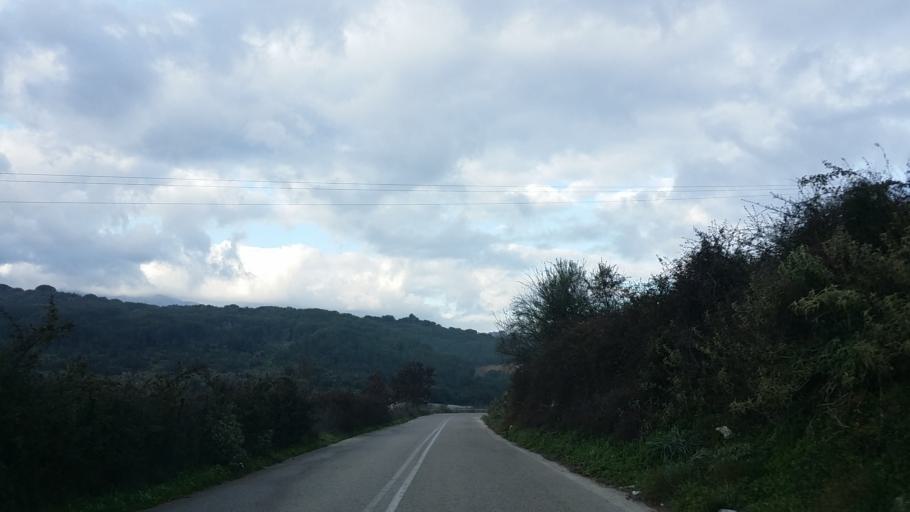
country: GR
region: West Greece
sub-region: Nomos Aitolias kai Akarnanias
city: Katouna
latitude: 38.7770
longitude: 21.1294
